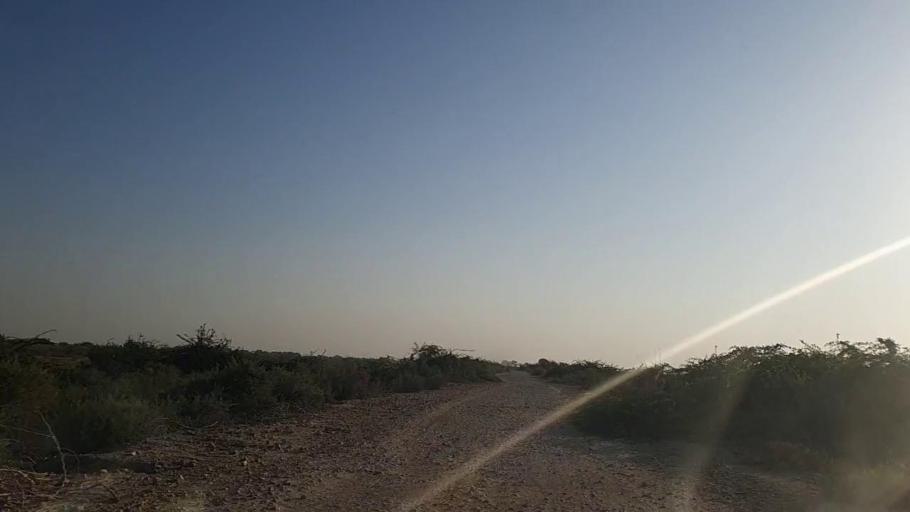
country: PK
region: Sindh
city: Jati
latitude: 24.4391
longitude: 68.1932
